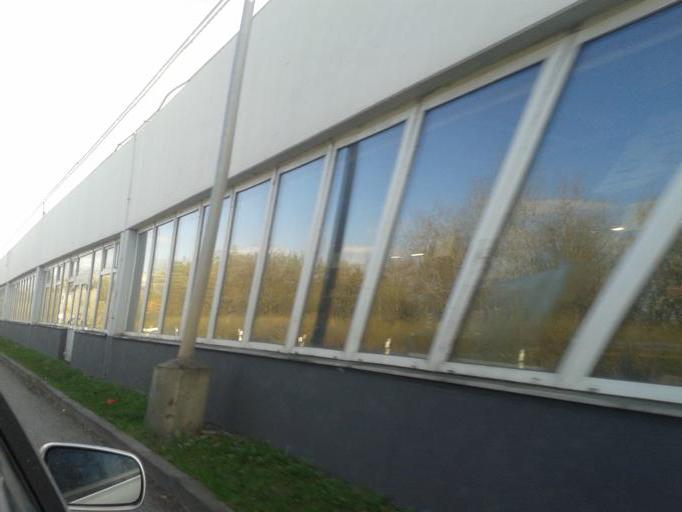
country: CZ
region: Central Bohemia
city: Hostivice
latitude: 50.0536
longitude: 14.2996
